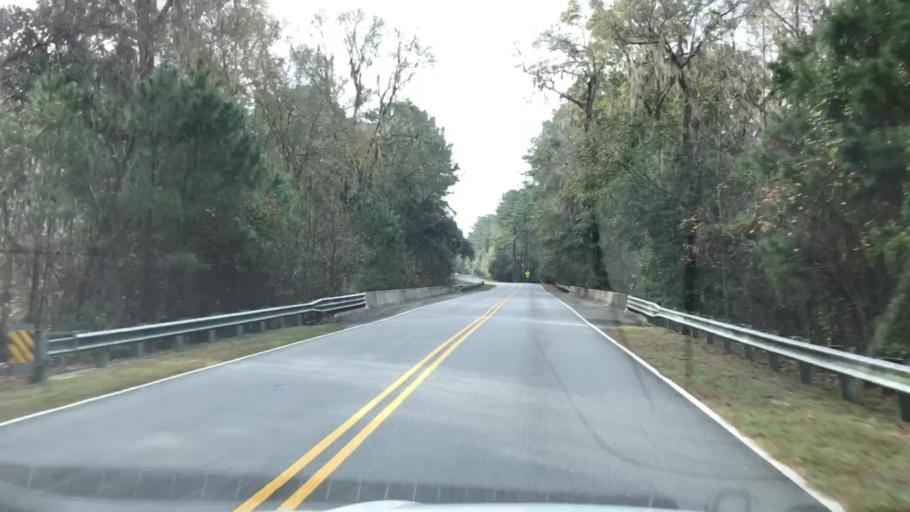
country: US
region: South Carolina
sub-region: Beaufort County
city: Bluffton
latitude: 32.2813
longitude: -80.9275
